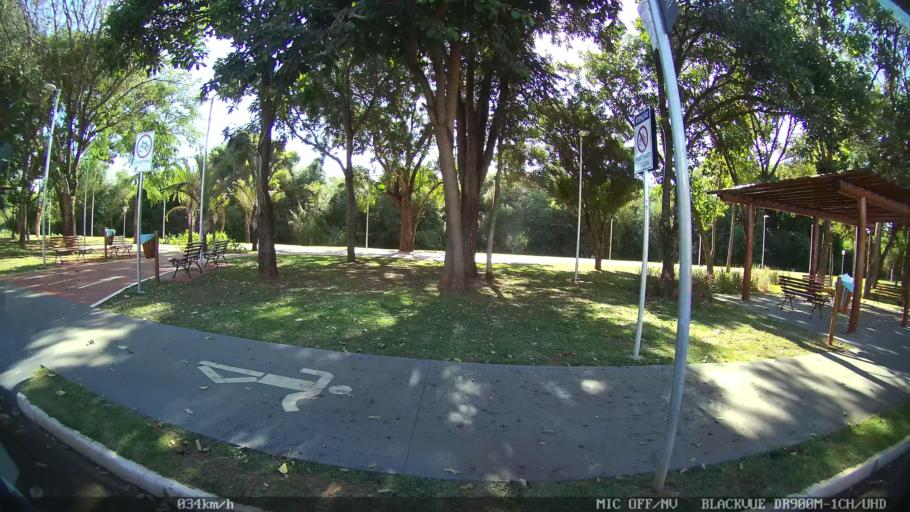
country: BR
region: Sao Paulo
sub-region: Olimpia
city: Olimpia
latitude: -20.7300
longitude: -48.9188
